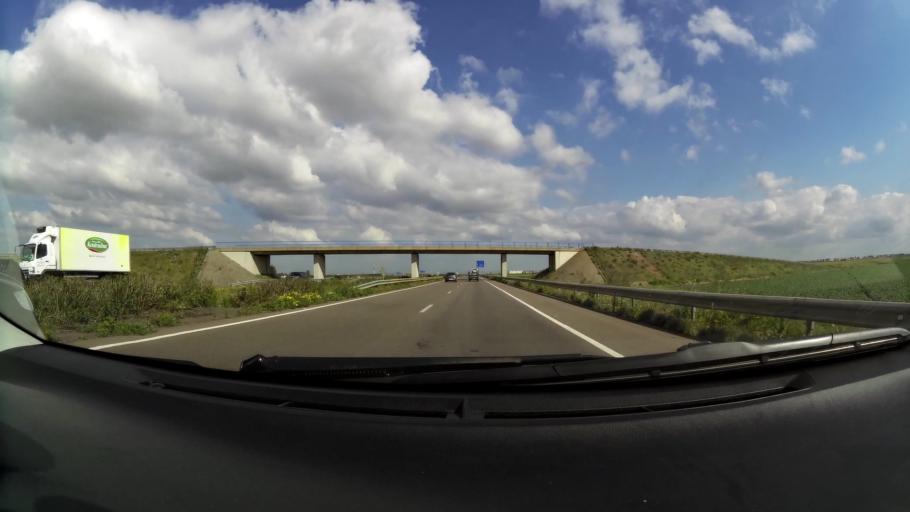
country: MA
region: Chaouia-Ouardigha
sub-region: Settat Province
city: Berrechid
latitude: 33.3070
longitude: -7.5857
